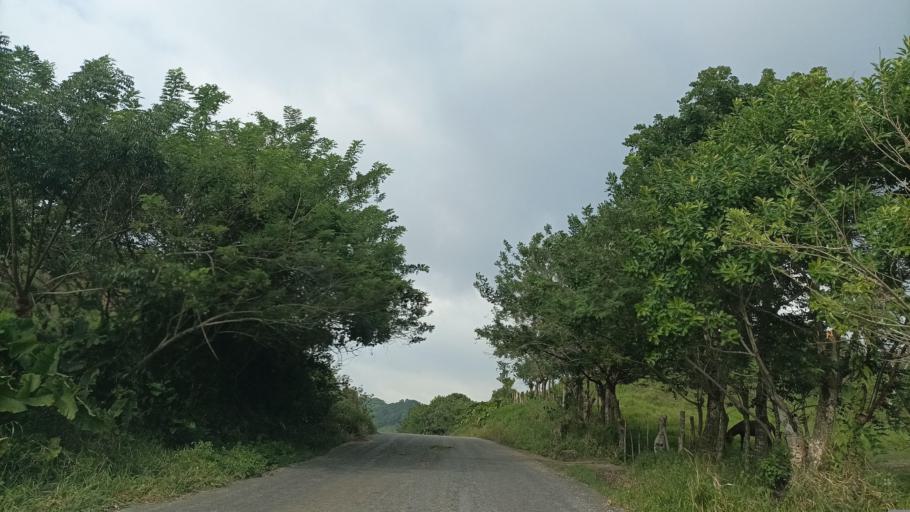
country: MX
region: Veracruz
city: Allende
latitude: 18.1120
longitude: -94.2920
